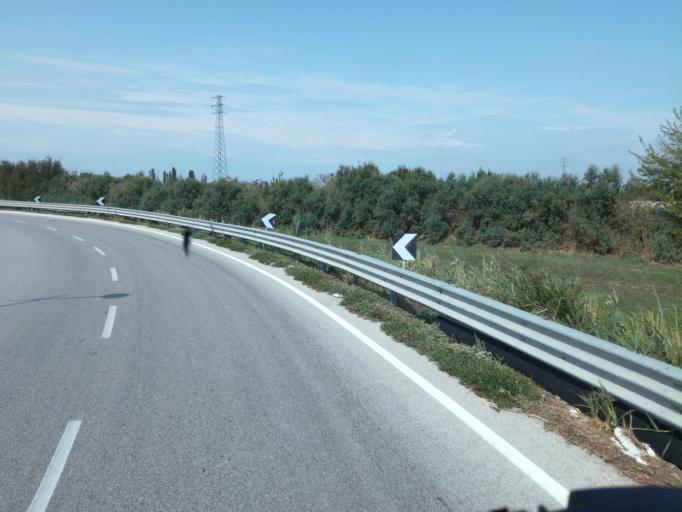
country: IT
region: Veneto
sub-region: Provincia di Rovigo
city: Loreo
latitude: 45.0524
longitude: 12.1540
